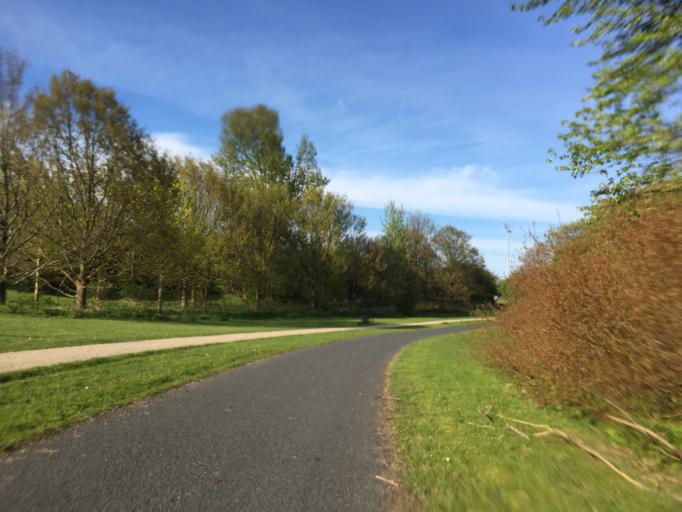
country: DK
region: Capital Region
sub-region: Kobenhavn
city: Vanlose
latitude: 55.7160
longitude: 12.4881
